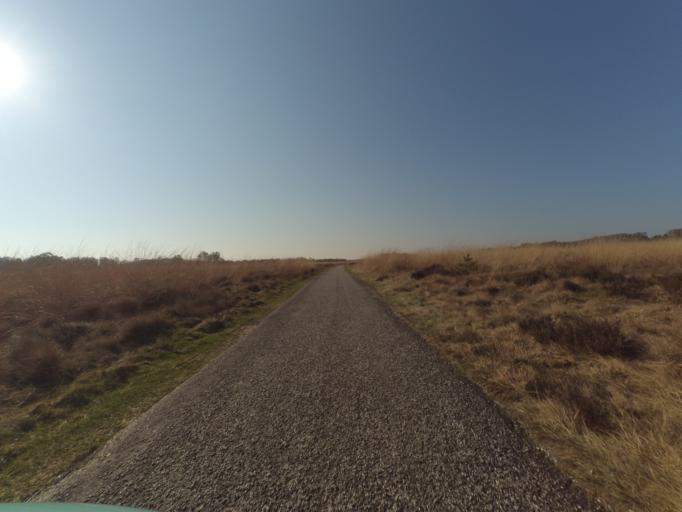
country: NL
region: Gelderland
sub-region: Gemeente Arnhem
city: Hoogkamp
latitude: 52.0661
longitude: 5.8470
